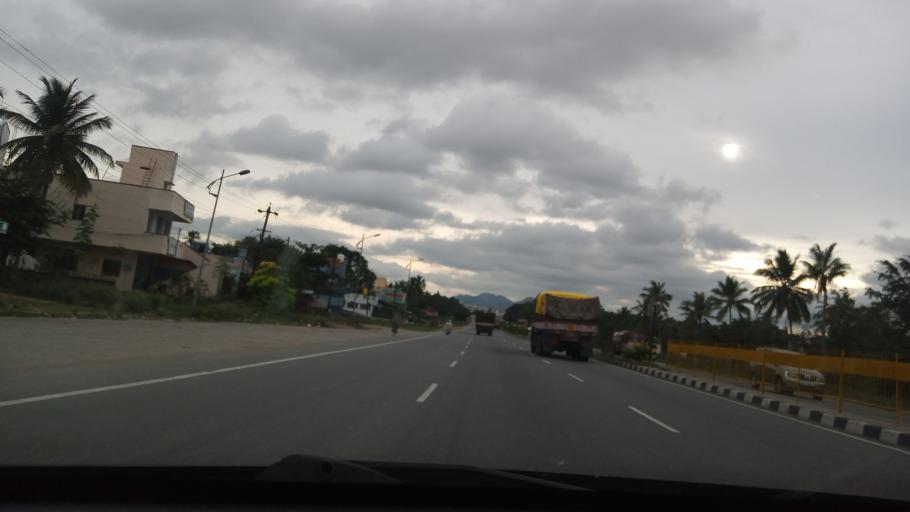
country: IN
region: Tamil Nadu
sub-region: Krishnagiri
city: Krishnagiri
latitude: 12.5422
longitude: 78.3100
